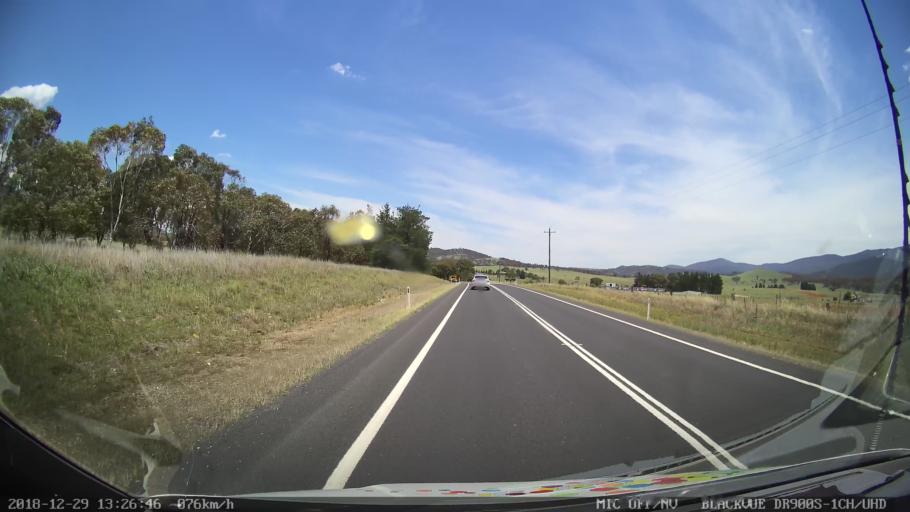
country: AU
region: New South Wales
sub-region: Cooma-Monaro
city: Cooma
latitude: -35.8592
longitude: 149.1581
